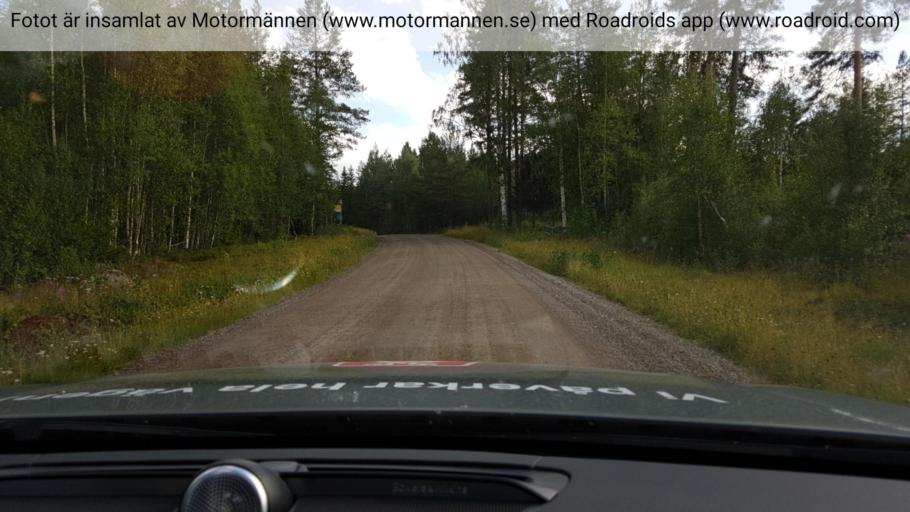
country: SE
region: Vaesterbotten
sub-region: Dorotea Kommun
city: Dorotea
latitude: 63.9444
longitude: 16.0771
